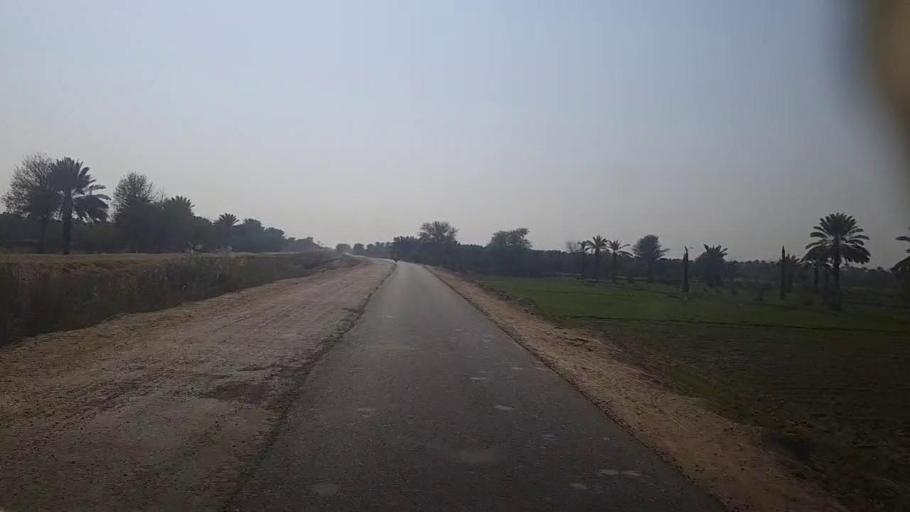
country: PK
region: Sindh
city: Khairpur
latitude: 27.4670
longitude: 68.8189
